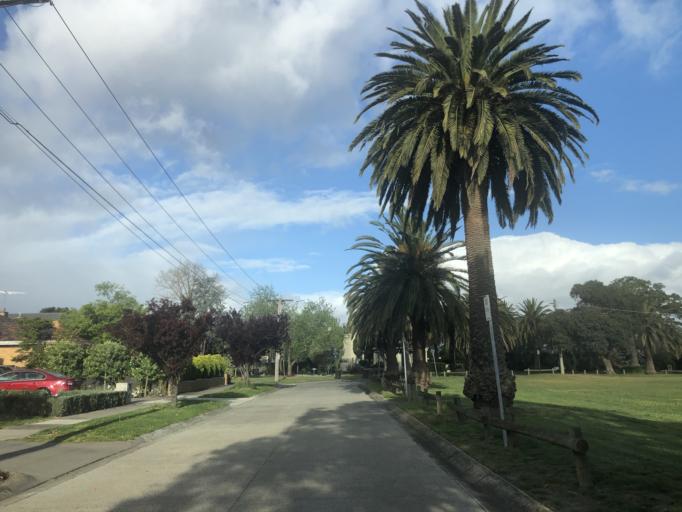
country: AU
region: Victoria
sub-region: Monash
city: Ashwood
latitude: -37.8789
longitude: 145.1265
